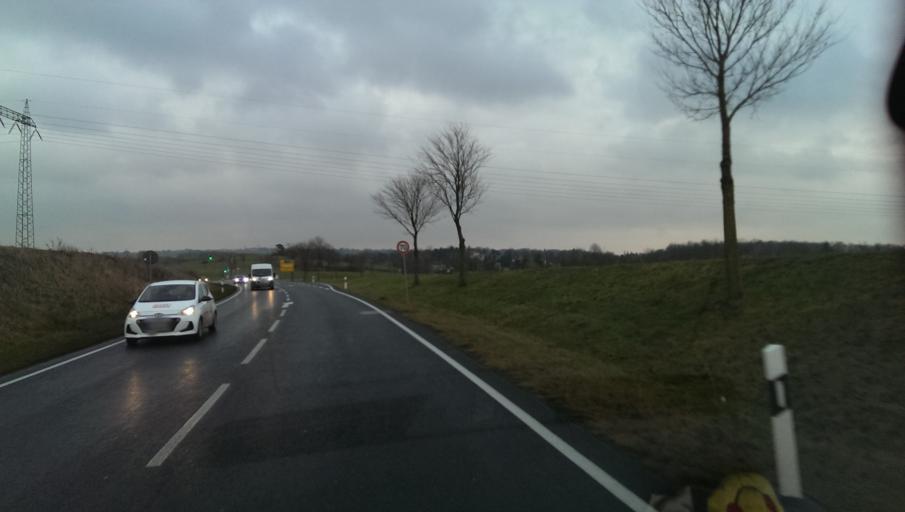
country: DE
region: Saxony
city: Moritzburg
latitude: 51.1405
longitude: 13.6526
